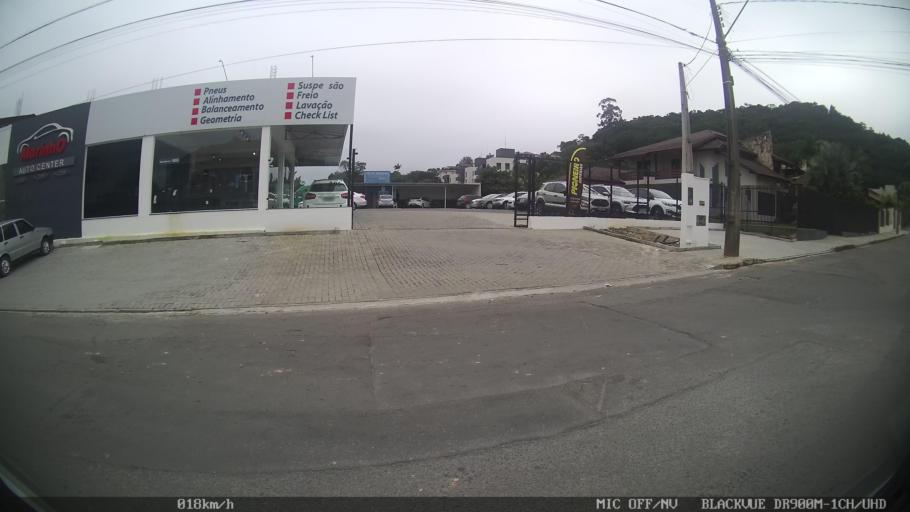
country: BR
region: Santa Catarina
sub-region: Joinville
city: Joinville
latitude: -26.2800
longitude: -48.8334
